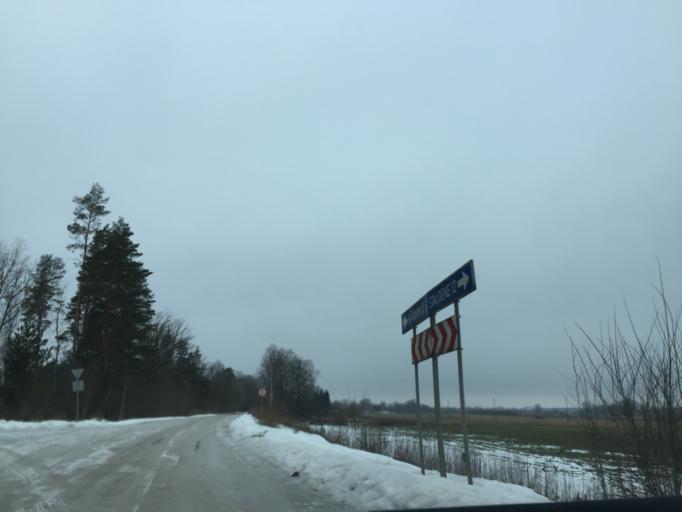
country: LV
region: Ozolnieku
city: Ozolnieki
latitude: 56.6302
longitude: 23.8177
